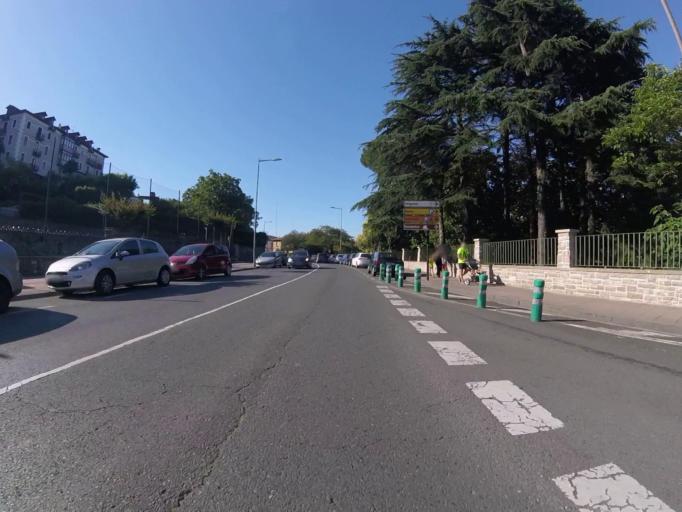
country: ES
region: Basque Country
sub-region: Provincia de Guipuzcoa
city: Fuenterrabia
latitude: 43.3628
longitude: -1.7898
